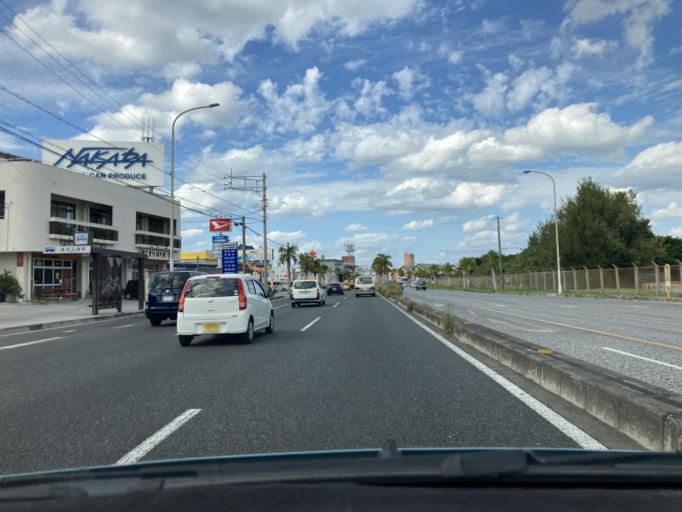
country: JP
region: Okinawa
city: Chatan
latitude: 26.3527
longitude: 127.7461
